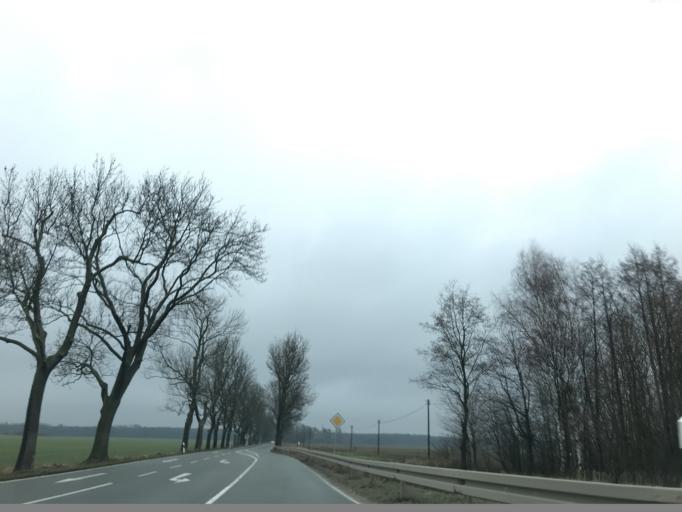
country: DE
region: Brandenburg
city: Brieselang
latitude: 52.6038
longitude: 12.9599
